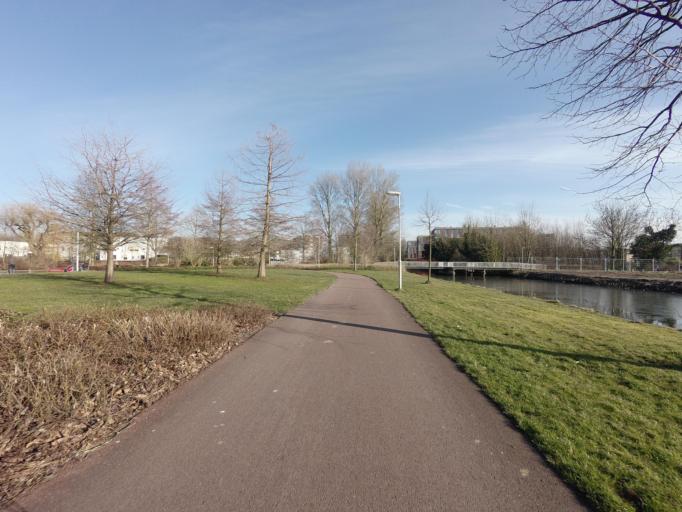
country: NL
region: South Holland
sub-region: Gemeente Gorinchem
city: Gorinchem
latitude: 51.8385
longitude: 4.9535
